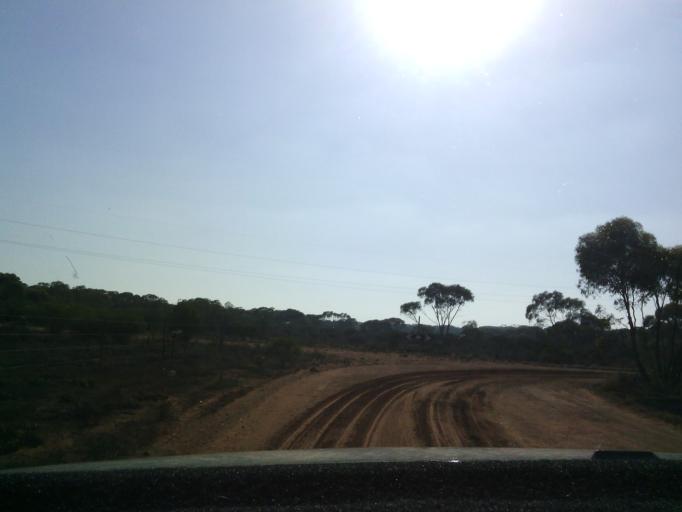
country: AU
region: South Australia
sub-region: Berri and Barmera
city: Monash
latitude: -34.2248
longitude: 140.5886
